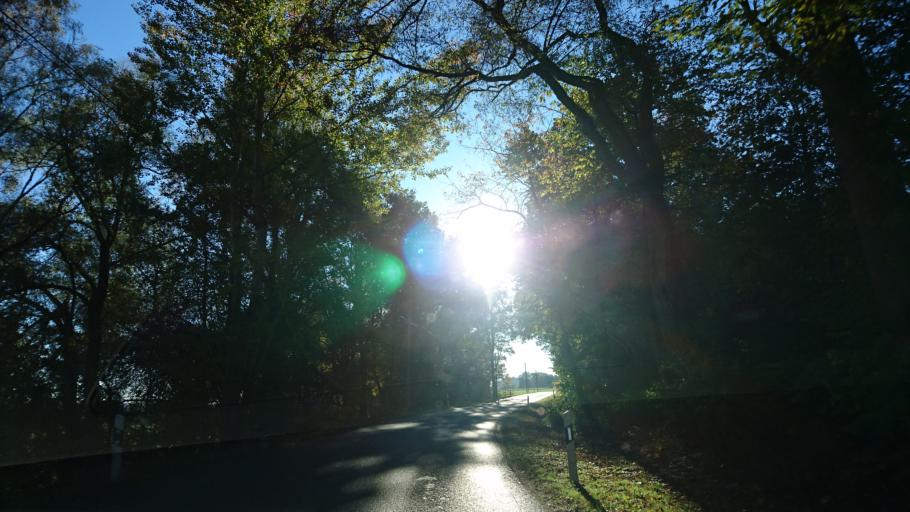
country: DE
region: Bavaria
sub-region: Swabia
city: Zusmarshausen
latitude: 48.3969
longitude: 10.5832
